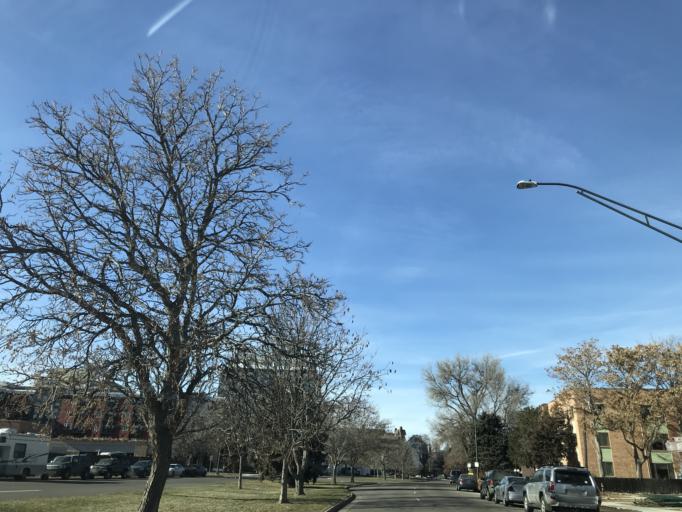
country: US
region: Colorado
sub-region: Arapahoe County
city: Glendale
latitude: 39.7339
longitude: -104.9361
